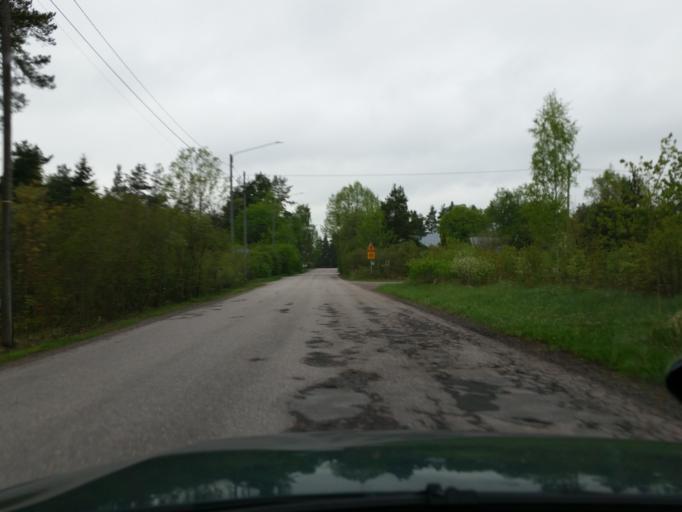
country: FI
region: Uusimaa
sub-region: Raaseporin
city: Inga
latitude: 60.1355
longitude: 23.8680
